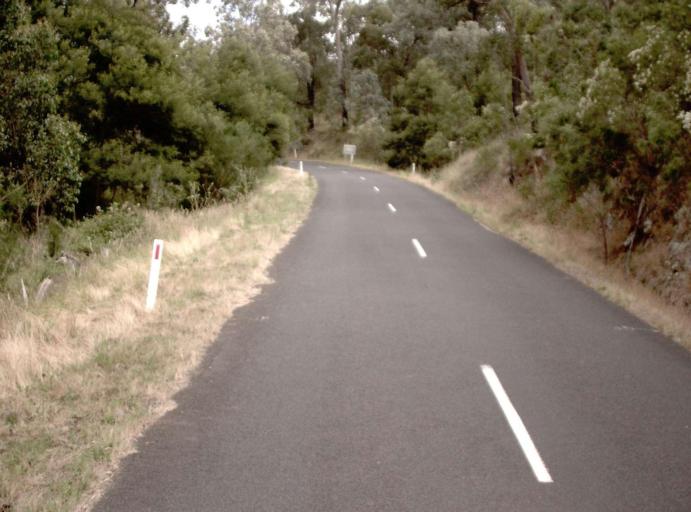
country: AU
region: Victoria
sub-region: Wellington
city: Heyfield
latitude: -37.7575
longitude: 146.6691
